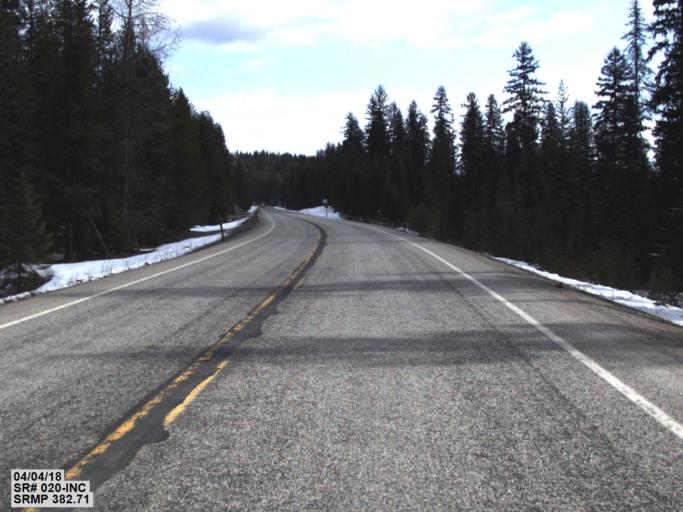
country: US
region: Washington
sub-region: Stevens County
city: Colville
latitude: 48.6493
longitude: -117.5070
